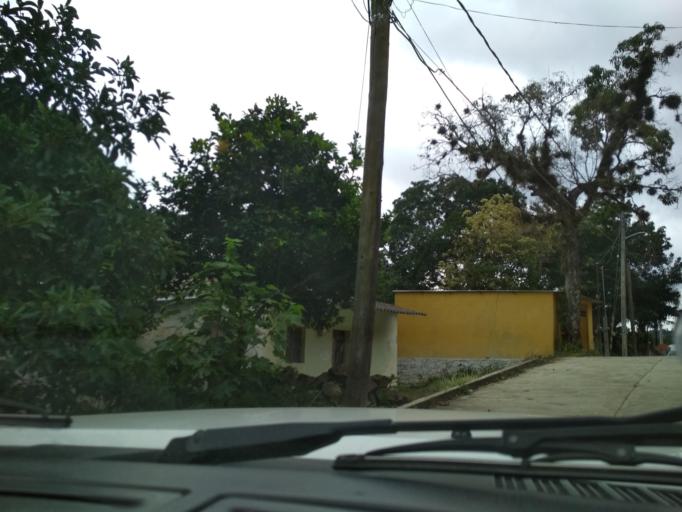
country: MX
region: Veracruz
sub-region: Naolinco
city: El Espinal
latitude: 19.5880
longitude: -96.8759
